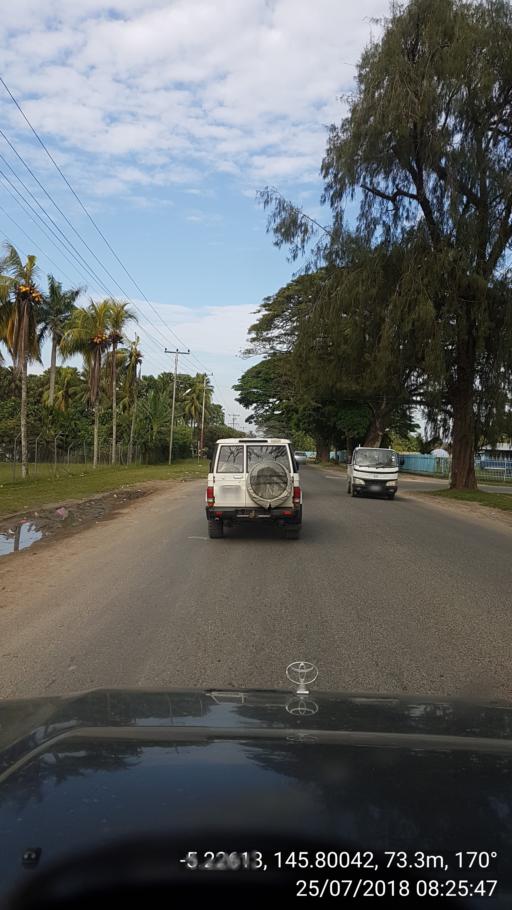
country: PG
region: Madang
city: Madang
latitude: -5.2260
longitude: 145.8006
